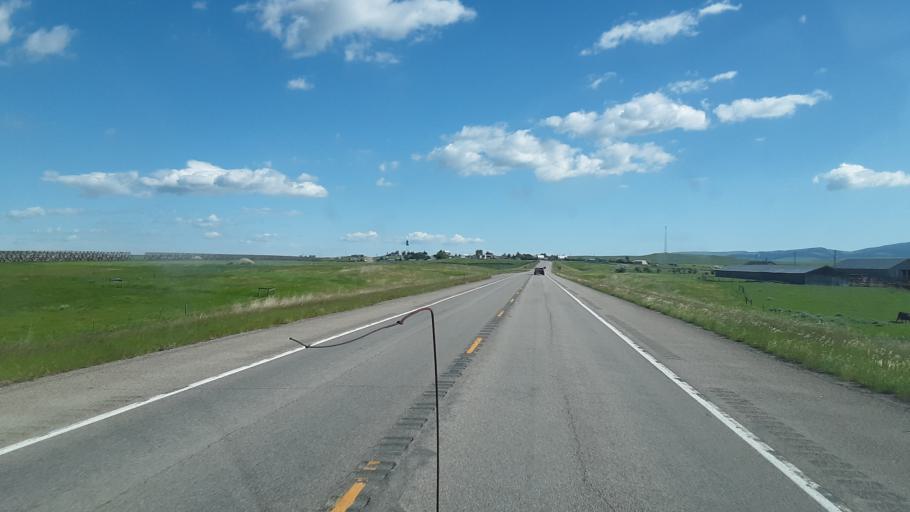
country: US
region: Montana
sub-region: Wheatland County
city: Harlowton
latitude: 46.6661
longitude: -109.7554
